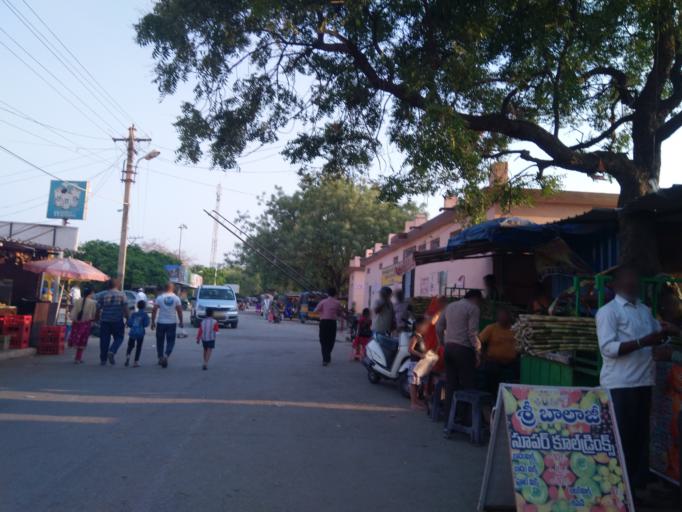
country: IN
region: Telangana
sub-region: Rangareddi
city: Sriramnagar
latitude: 17.3577
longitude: 78.2997
